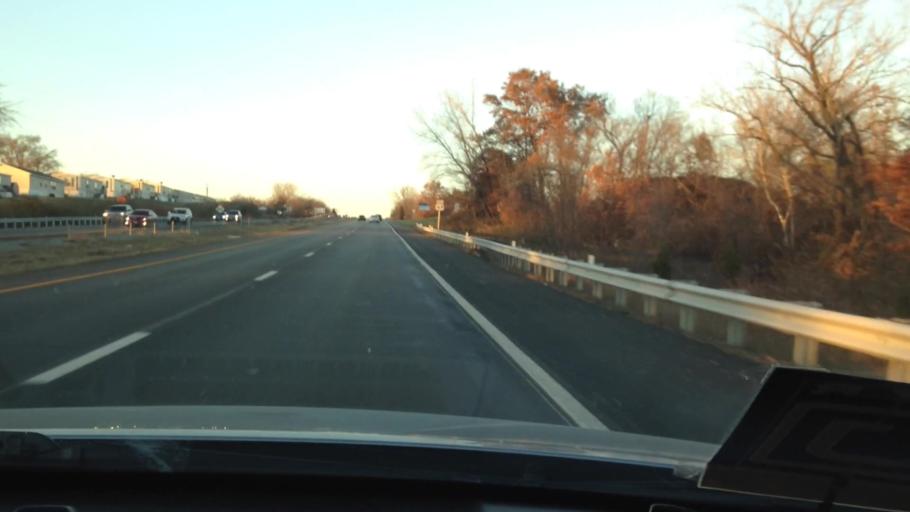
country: US
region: Missouri
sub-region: Platte County
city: Riverside
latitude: 39.1995
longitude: -94.5897
